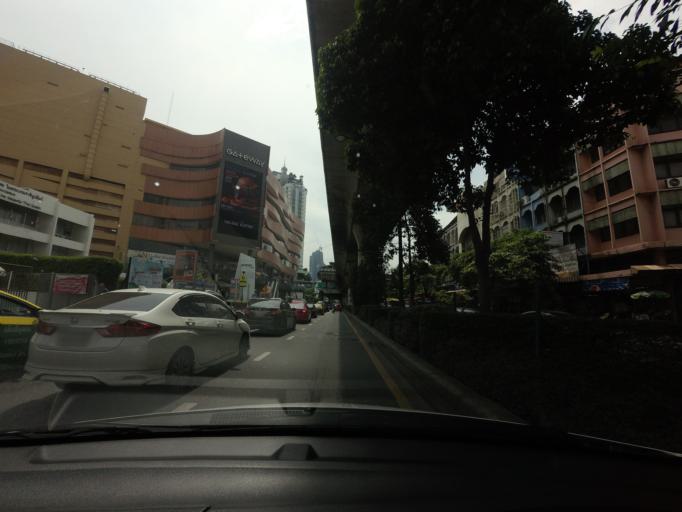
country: TH
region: Bangkok
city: Watthana
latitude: 13.7186
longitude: 100.5864
